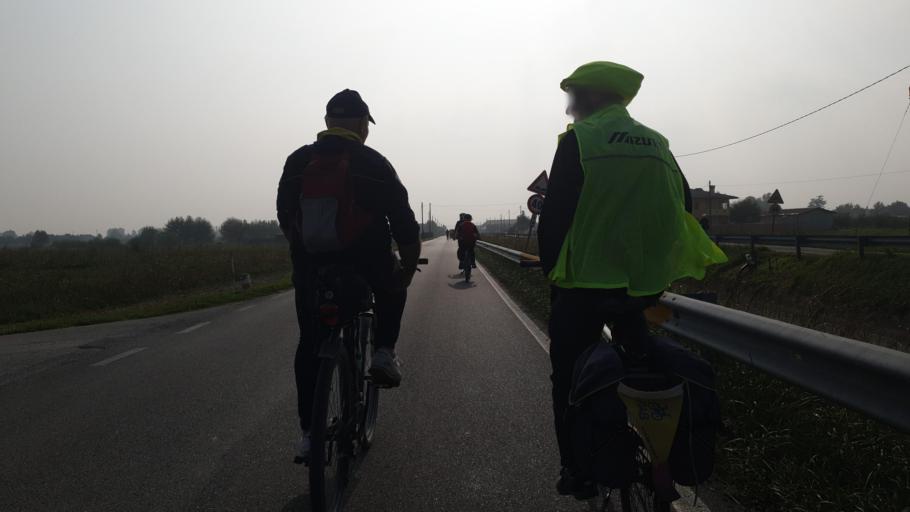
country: IT
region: Veneto
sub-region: Provincia di Padova
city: Corte
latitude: 45.3025
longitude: 12.0774
